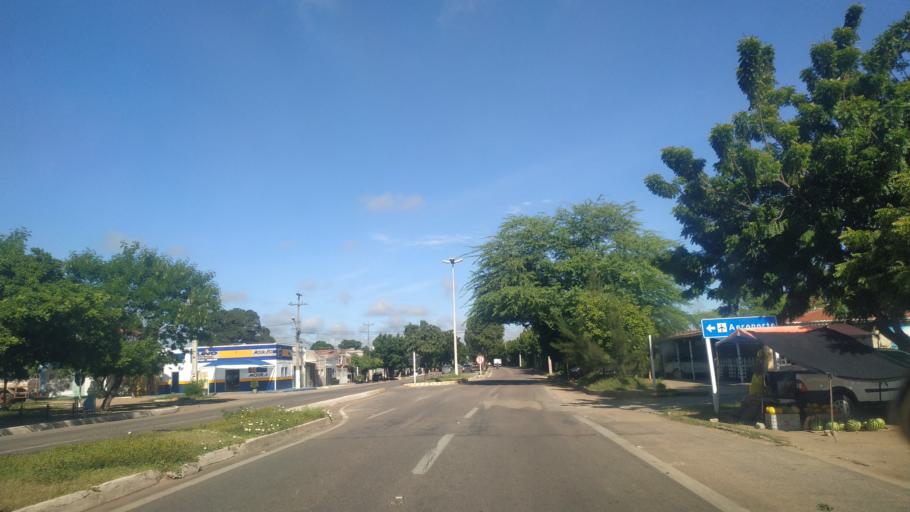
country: BR
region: Rio Grande do Norte
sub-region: Mossoro
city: Mossoro
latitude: -5.1917
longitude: -37.3625
